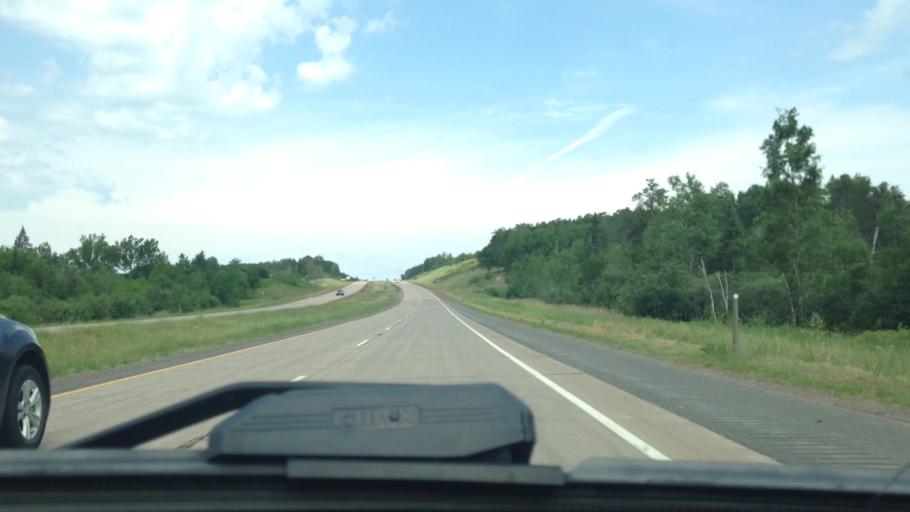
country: US
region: Wisconsin
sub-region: Douglas County
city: Lake Nebagamon
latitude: 46.3258
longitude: -91.8188
